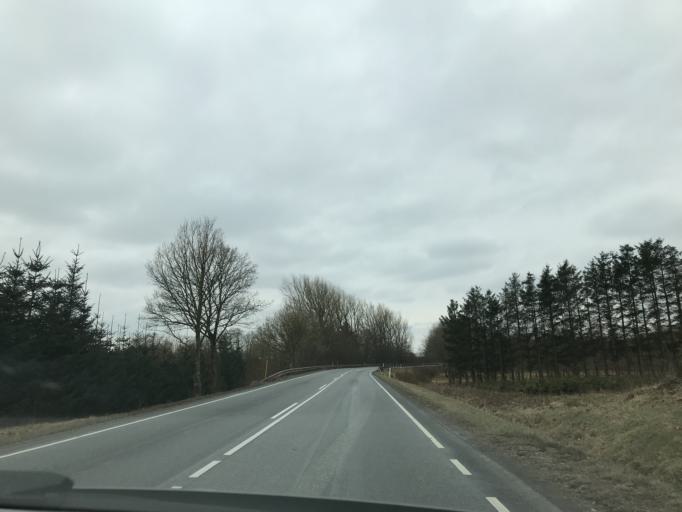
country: DK
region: South Denmark
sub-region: Varde Kommune
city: Olgod
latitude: 55.8131
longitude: 8.6614
